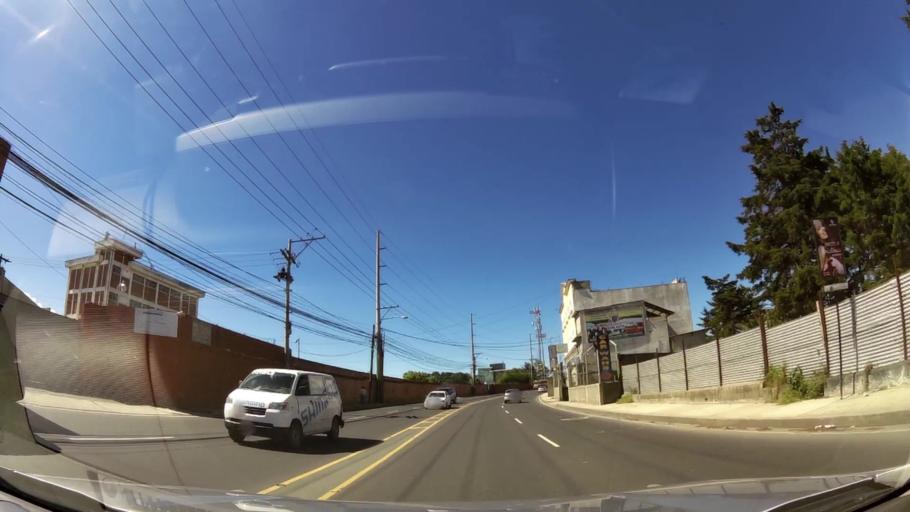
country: GT
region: Guatemala
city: San Jose Pinula
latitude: 14.5418
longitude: -90.4510
